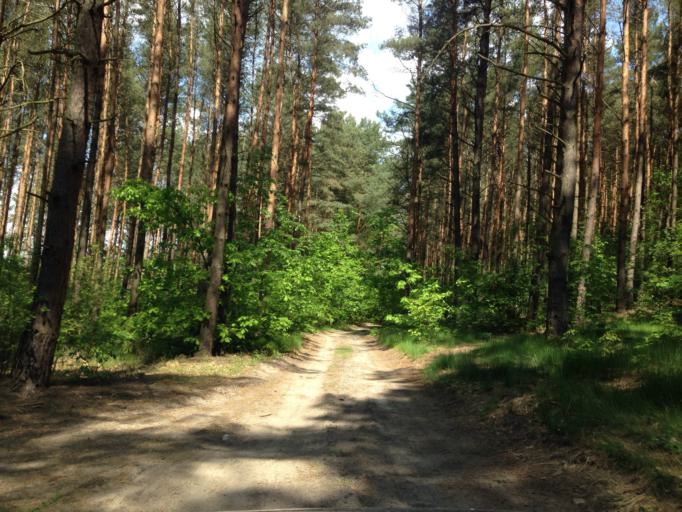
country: PL
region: Kujawsko-Pomorskie
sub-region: Powiat brodnicki
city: Brodnica
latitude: 53.3290
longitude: 19.3578
